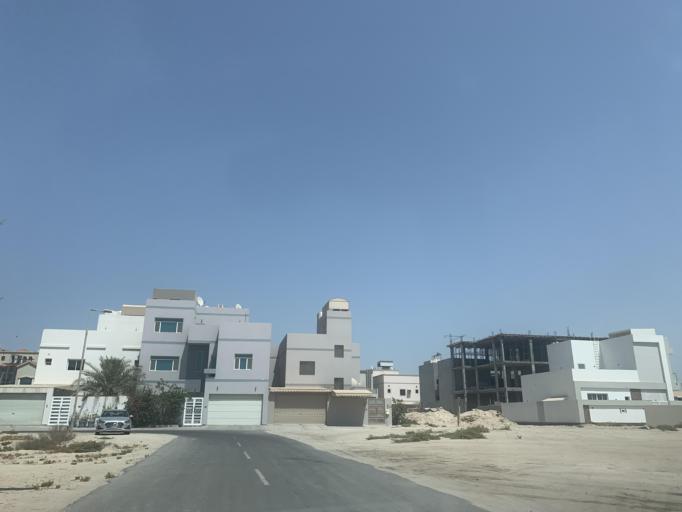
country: BH
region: Manama
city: Jidd Hafs
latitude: 26.2289
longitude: 50.5144
